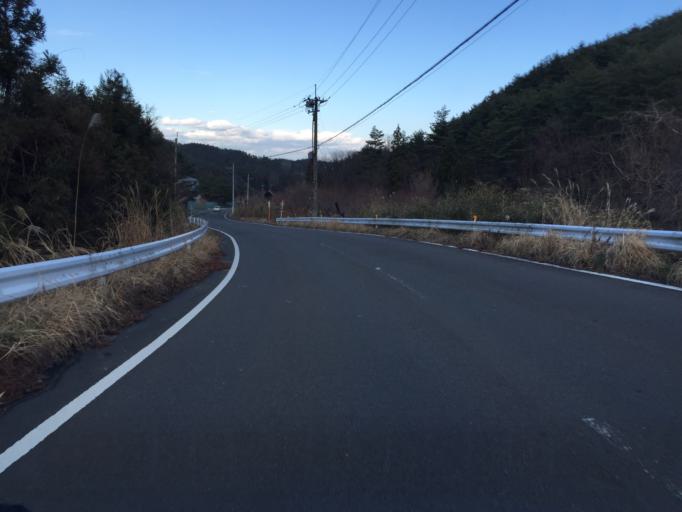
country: JP
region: Fukushima
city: Fukushima-shi
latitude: 37.7002
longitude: 140.3912
